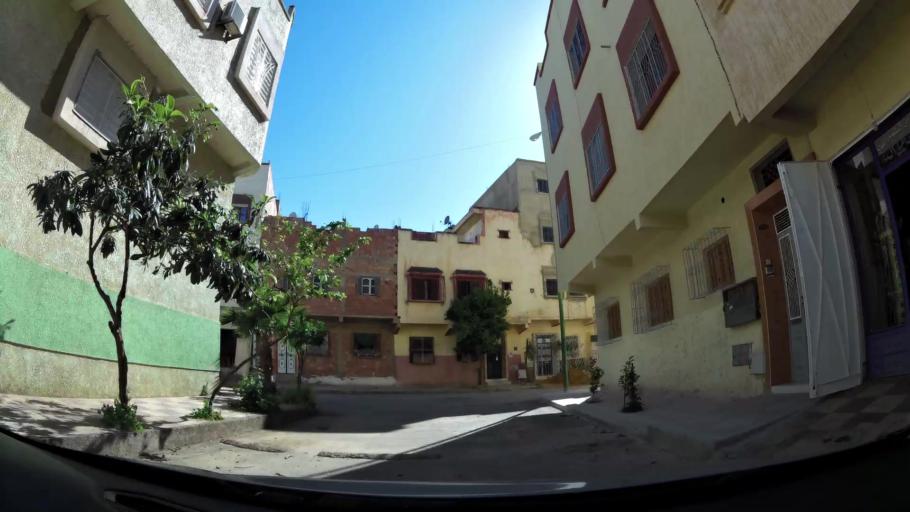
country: MA
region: Meknes-Tafilalet
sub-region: Meknes
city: Meknes
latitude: 33.8760
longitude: -5.5774
